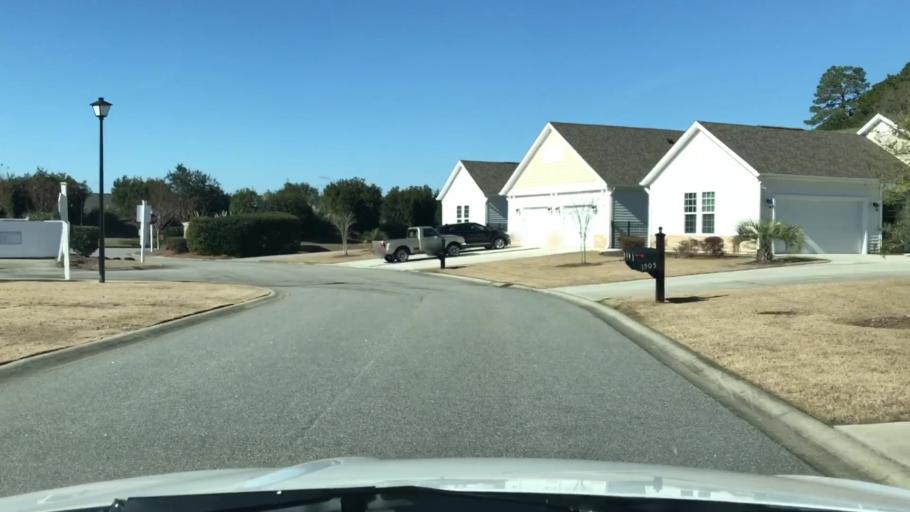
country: US
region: South Carolina
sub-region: Horry County
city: Socastee
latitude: 33.6462
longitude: -79.0367
